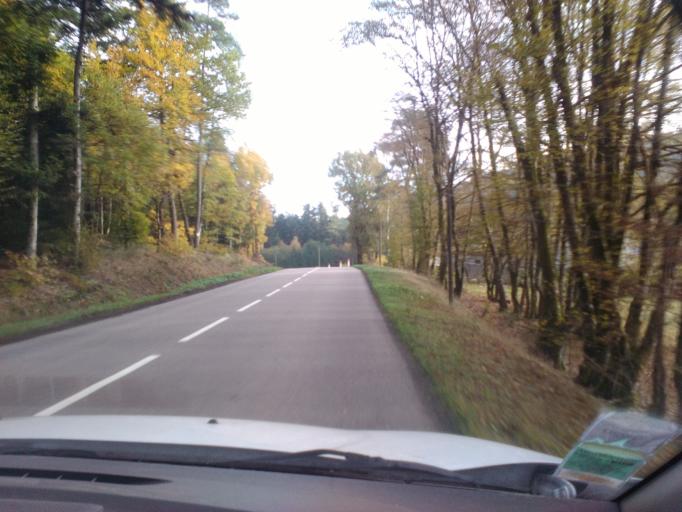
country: FR
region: Lorraine
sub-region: Departement des Vosges
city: Etival-Clairefontaine
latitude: 48.3895
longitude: 6.8093
